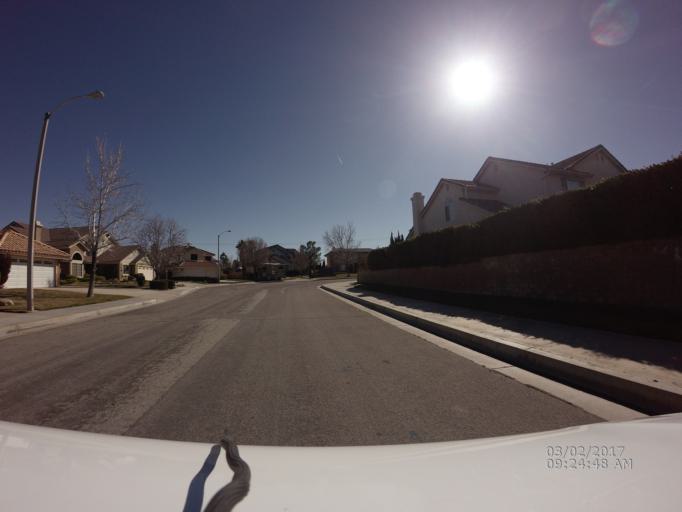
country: US
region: California
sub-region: Los Angeles County
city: Quartz Hill
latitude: 34.6377
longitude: -118.2200
